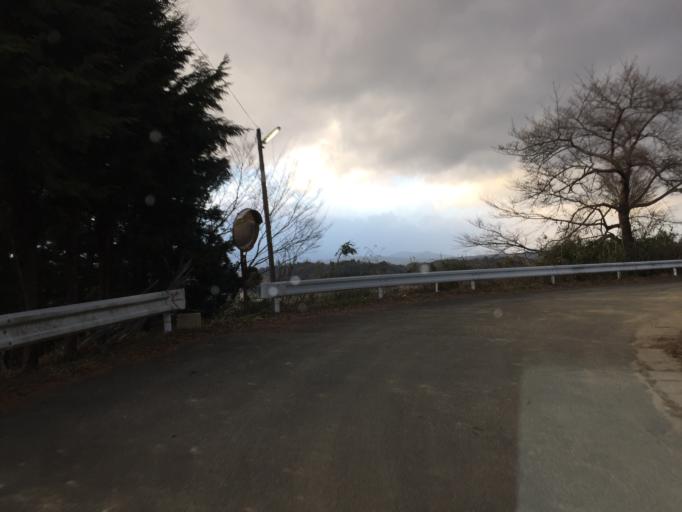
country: JP
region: Fukushima
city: Nihommatsu
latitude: 37.5574
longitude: 140.4409
